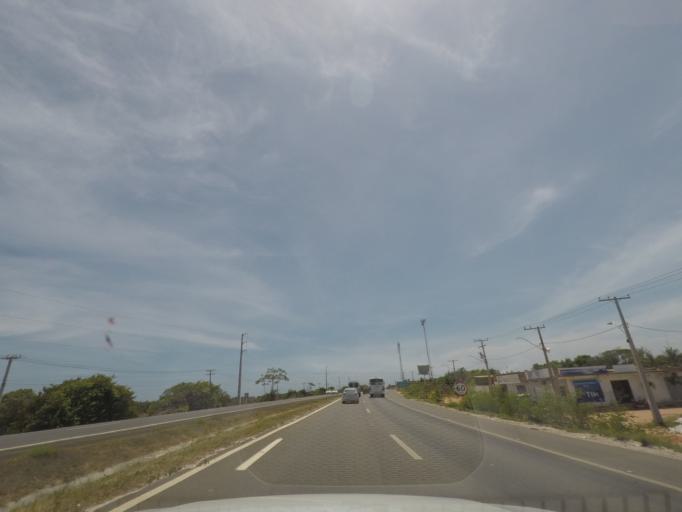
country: BR
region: Bahia
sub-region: Mata De Sao Joao
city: Mata de Sao Joao
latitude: -12.6019
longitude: -38.0468
